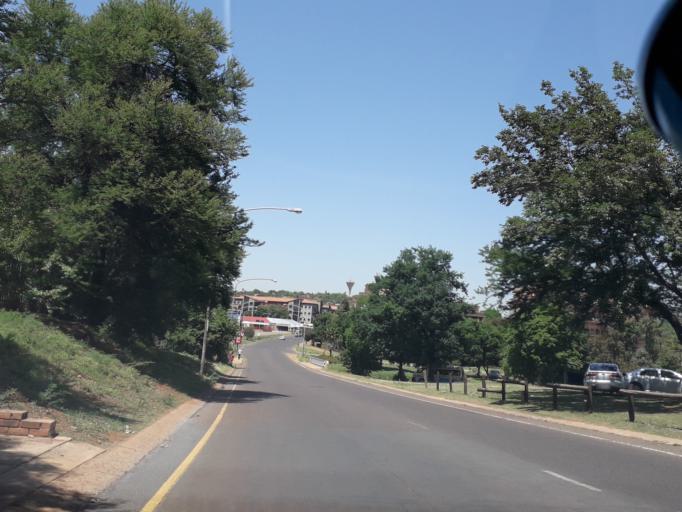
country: ZA
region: Gauteng
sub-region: City of Tshwane Metropolitan Municipality
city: Centurion
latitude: -25.8562
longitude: 28.1923
